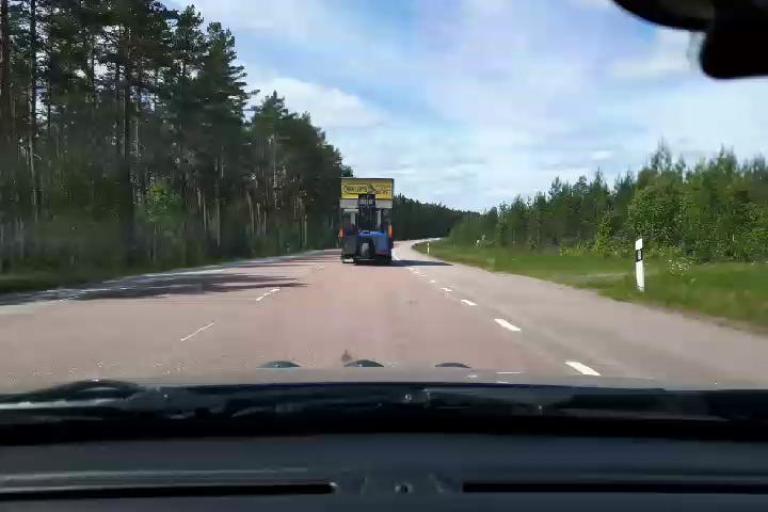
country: SE
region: Uppsala
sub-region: Osthammars Kommun
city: Bjorklinge
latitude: 60.1122
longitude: 17.5272
